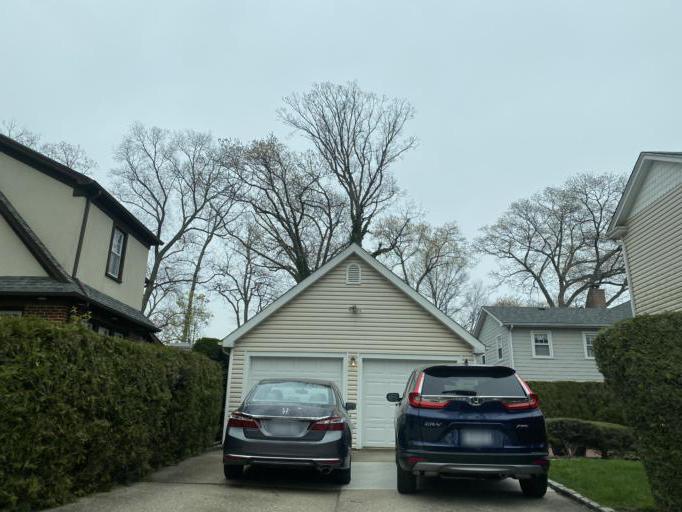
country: US
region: New York
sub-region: Nassau County
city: Bellerose
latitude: 40.7168
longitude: -73.7172
